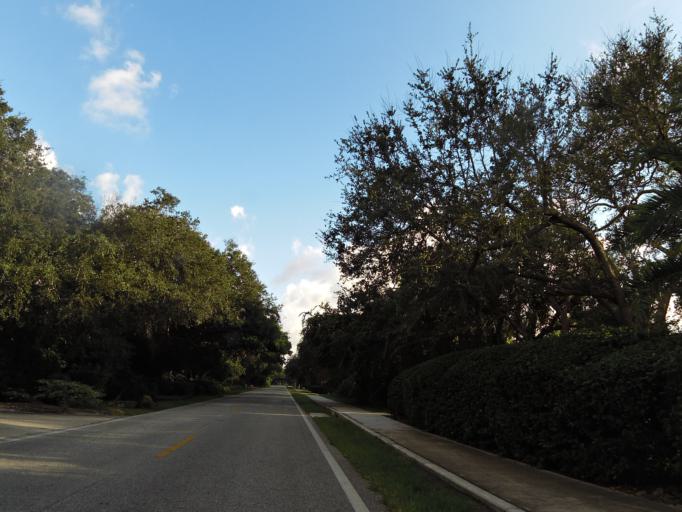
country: US
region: Florida
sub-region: Saint Johns County
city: Sawgrass
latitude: 30.1670
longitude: -81.3585
